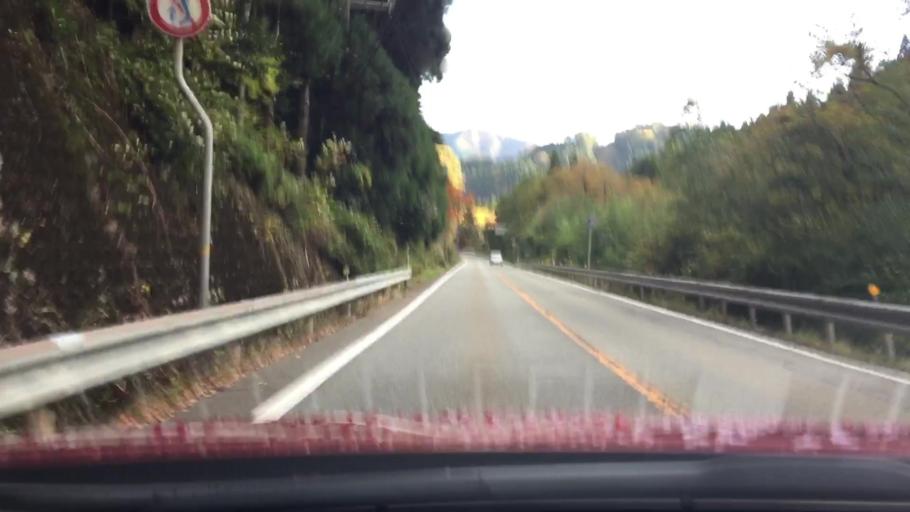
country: JP
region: Hyogo
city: Yamazakicho-nakabirose
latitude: 35.1799
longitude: 134.5358
